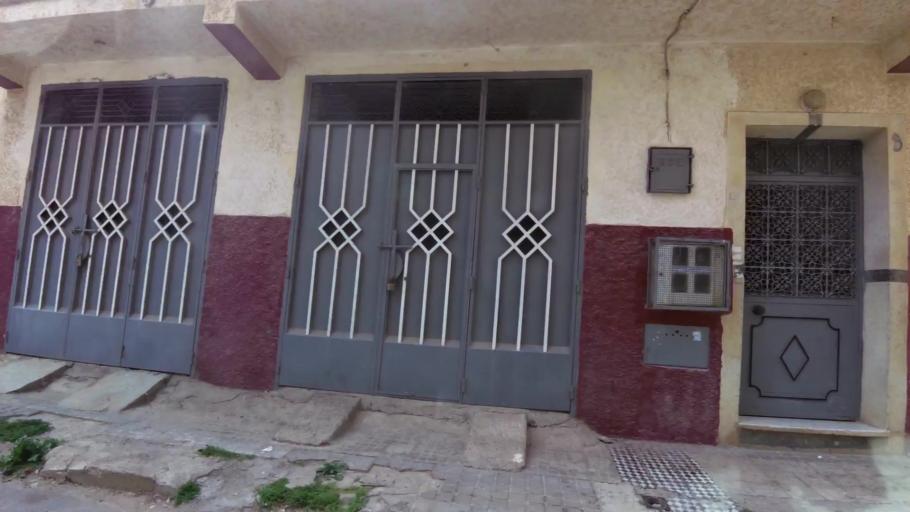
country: MA
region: Tanger-Tetouan
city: Tetouan
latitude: 35.5838
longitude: -5.3552
